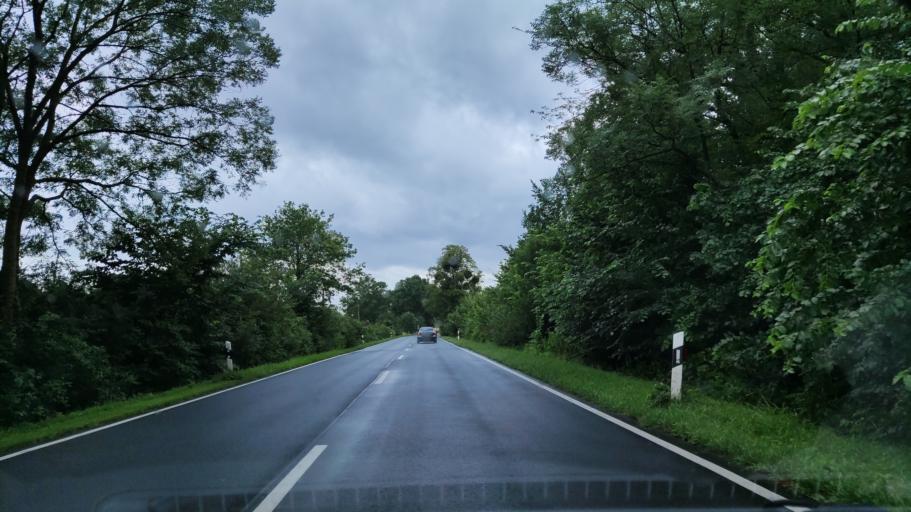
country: DE
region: North Rhine-Westphalia
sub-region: Regierungsbezirk Arnsberg
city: Hamm
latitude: 51.7229
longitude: 7.8509
